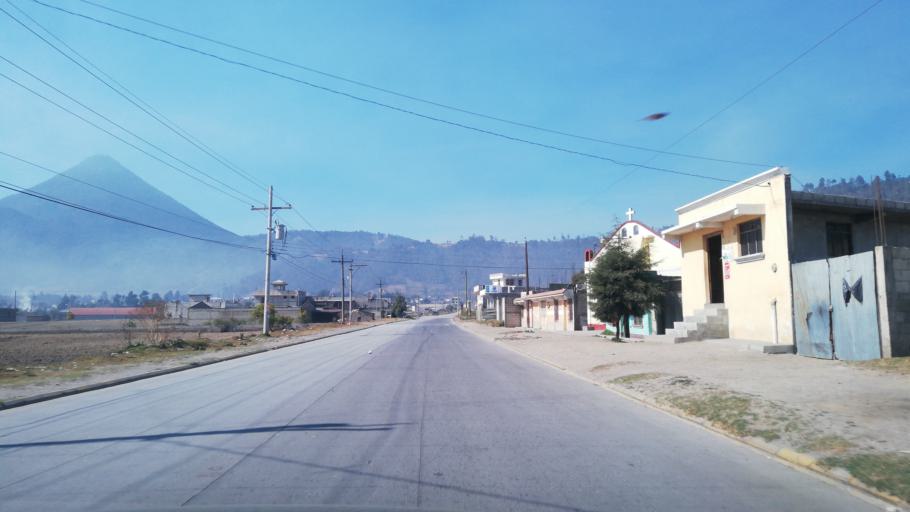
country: GT
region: Quetzaltenango
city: Quetzaltenango
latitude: 14.8141
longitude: -91.5488
